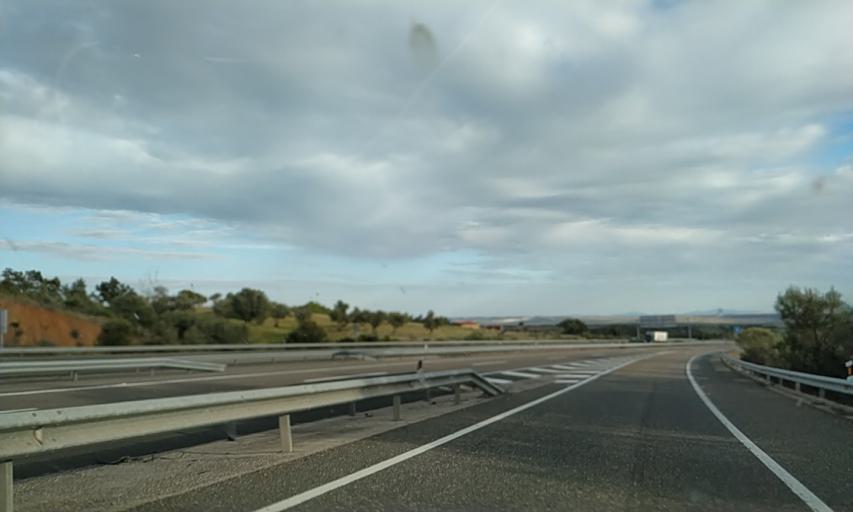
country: ES
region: Extremadura
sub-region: Provincia de Caceres
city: Casas de Millan
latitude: 39.8165
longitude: -6.3634
